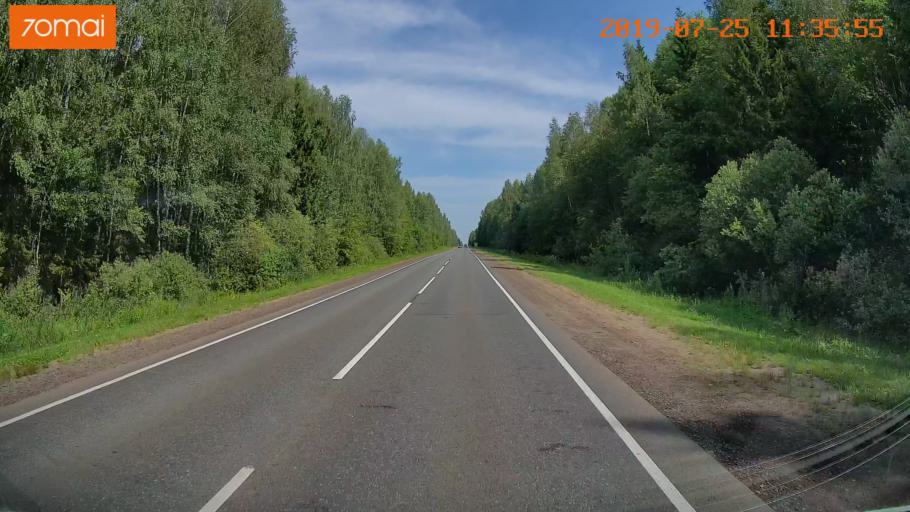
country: RU
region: Ivanovo
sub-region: Privolzhskiy Rayon
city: Ples
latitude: 57.4173
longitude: 41.4384
